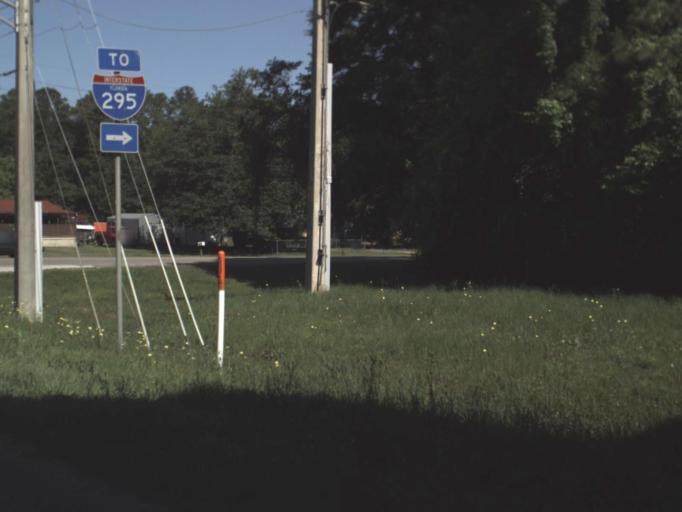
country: US
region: Florida
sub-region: Duval County
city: Jacksonville
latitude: 30.3229
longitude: -81.7704
